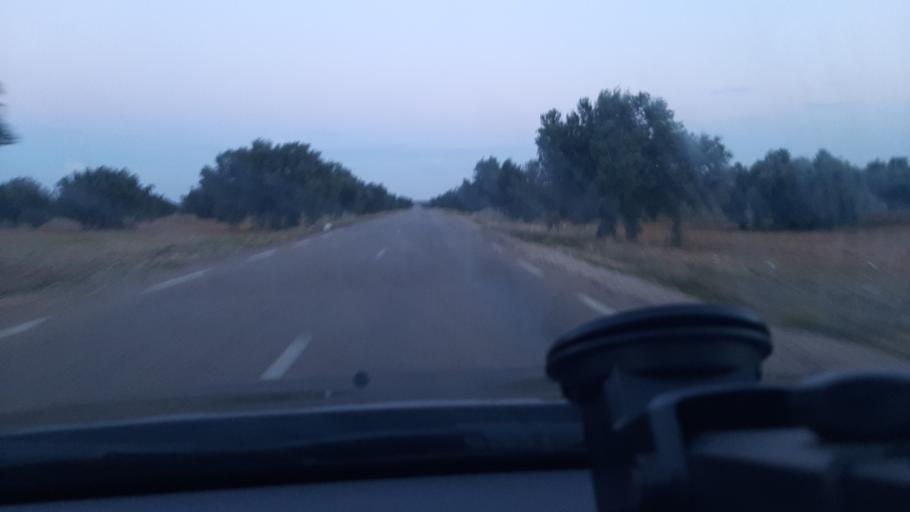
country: TN
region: Al Mahdiyah
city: Shurban
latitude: 35.0324
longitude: 10.5042
